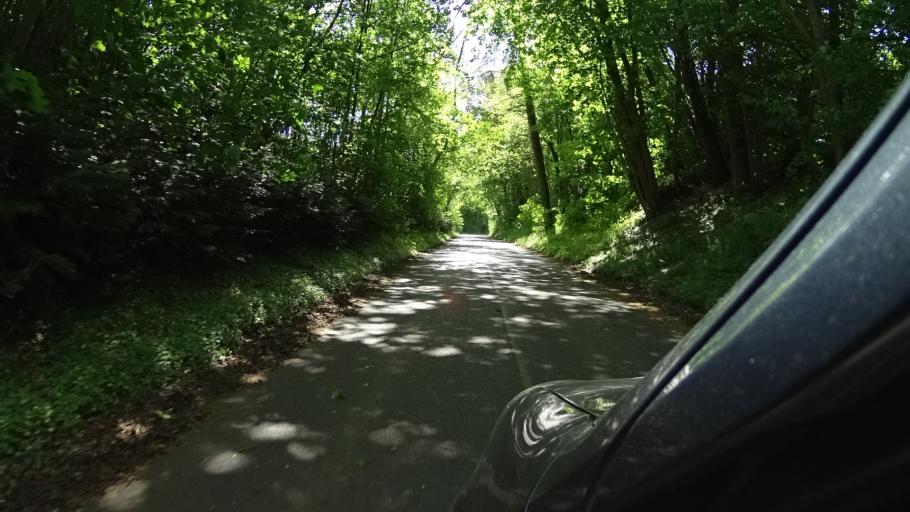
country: DK
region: South Denmark
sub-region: Vejle Kommune
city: Borkop
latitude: 55.6189
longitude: 9.6679
